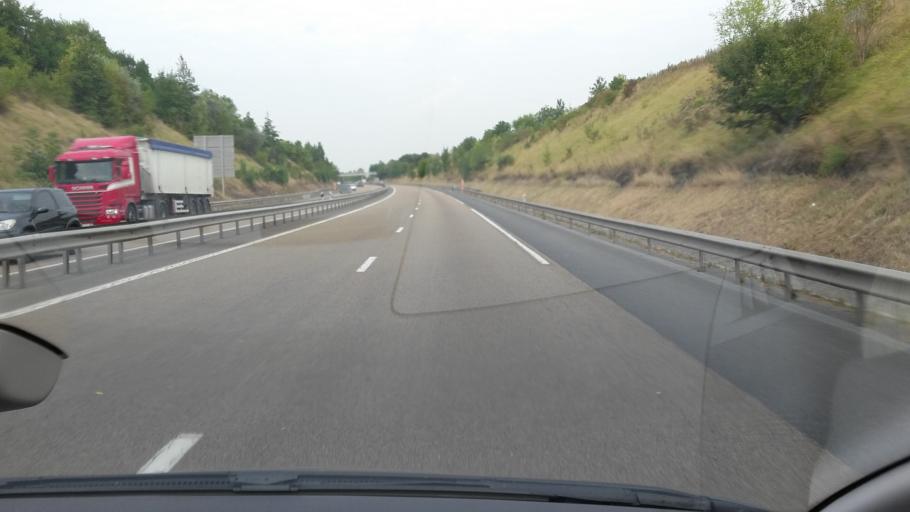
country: FR
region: Champagne-Ardenne
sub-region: Departement de la Marne
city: Witry-les-Reims
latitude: 49.2861
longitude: 4.1213
